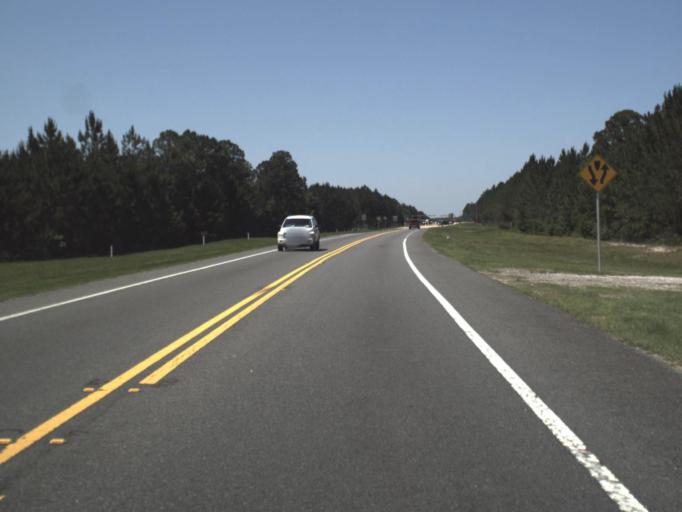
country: US
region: Florida
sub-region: Clay County
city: Lakeside
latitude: 30.1886
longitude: -81.8376
